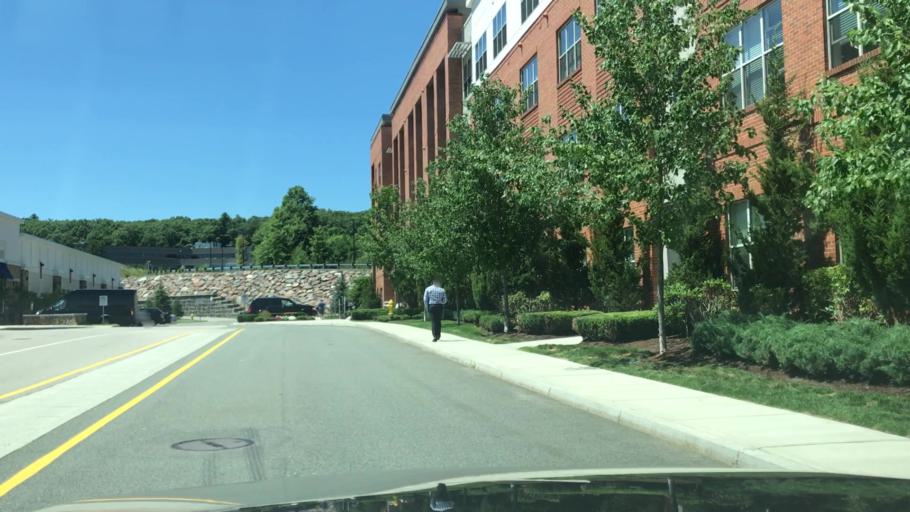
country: US
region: Massachusetts
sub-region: Norfolk County
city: Dedham
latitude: 42.2079
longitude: -71.1528
